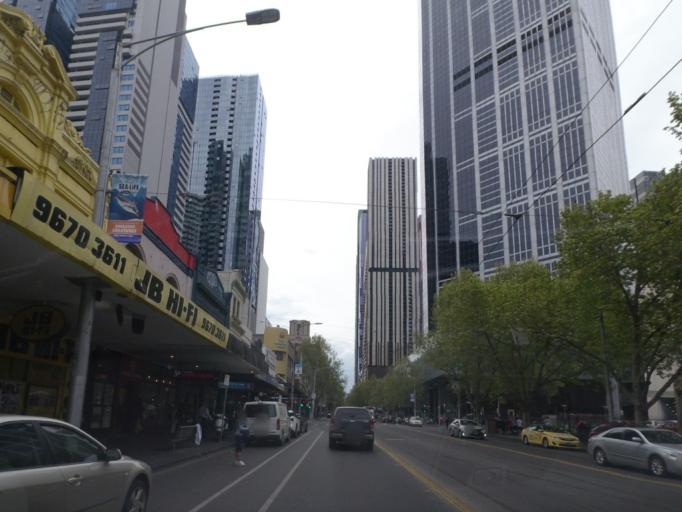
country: AU
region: Victoria
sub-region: Melbourne
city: Melbourne
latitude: -37.8117
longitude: 144.9621
